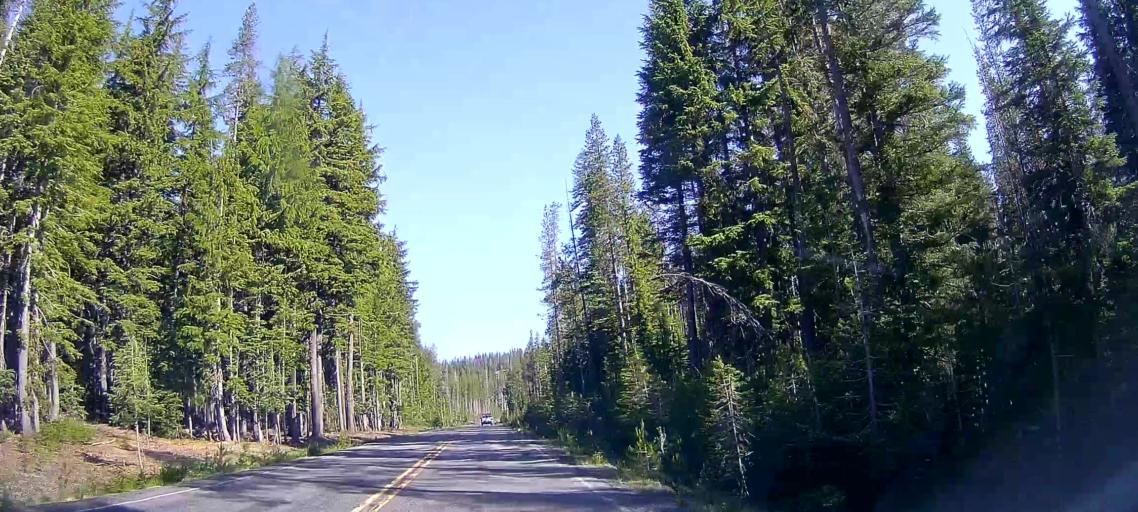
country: US
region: Oregon
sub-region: Jackson County
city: Shady Cove
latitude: 42.8386
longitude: -122.1448
